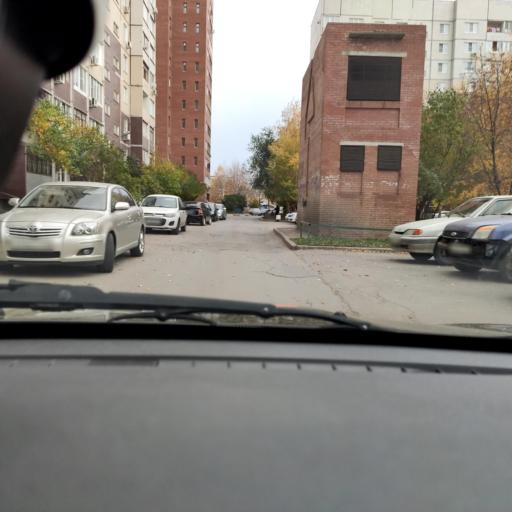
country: RU
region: Samara
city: Tol'yatti
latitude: 53.5468
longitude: 49.3219
